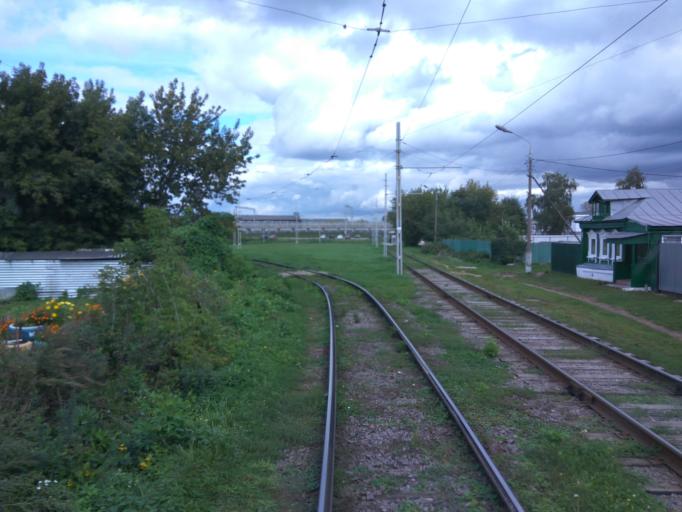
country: RU
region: Moskovskaya
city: Kolomna
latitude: 55.0994
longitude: 38.7777
